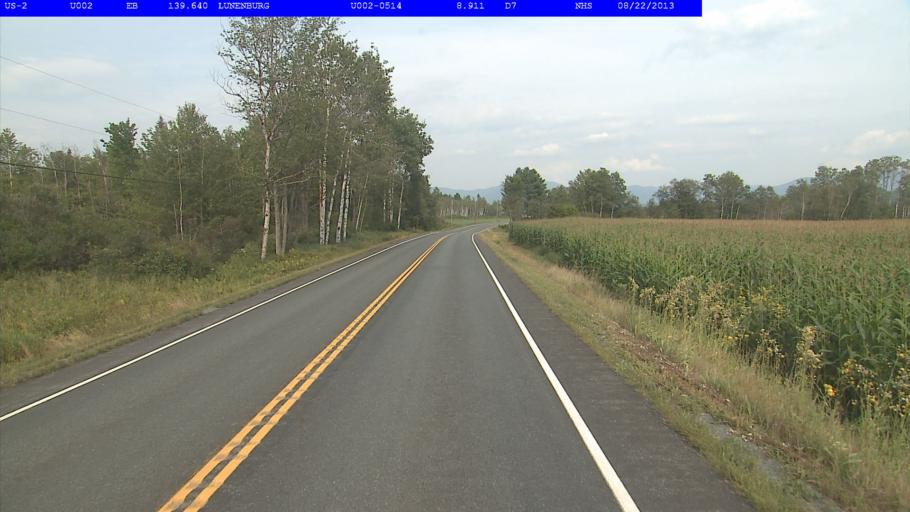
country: US
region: New Hampshire
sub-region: Coos County
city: Lancaster
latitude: 44.4868
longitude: -71.6140
